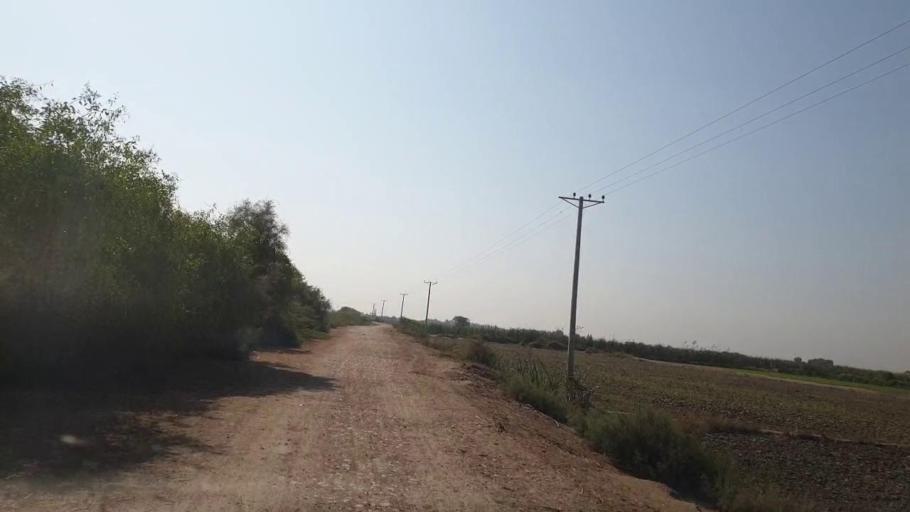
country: PK
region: Sindh
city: Thatta
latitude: 24.7307
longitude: 67.7940
